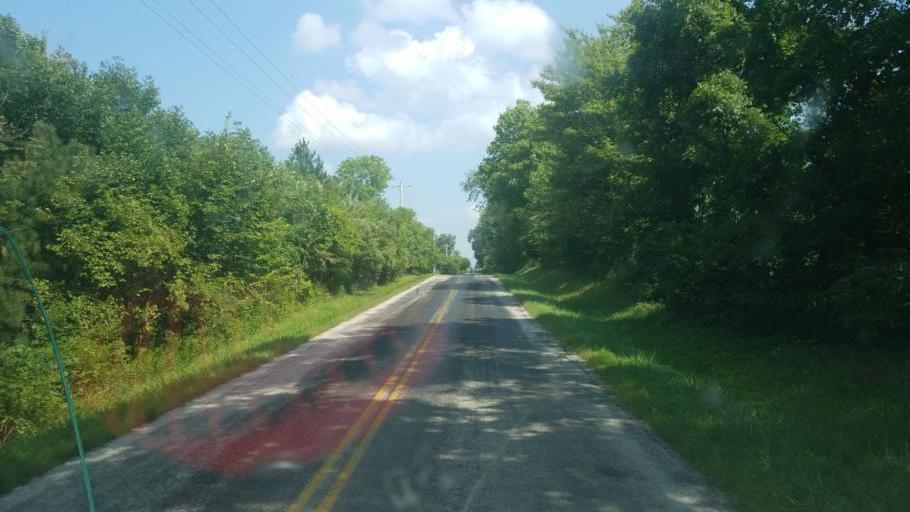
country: US
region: Ohio
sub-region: Huron County
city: New London
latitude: 41.0582
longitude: -82.3166
